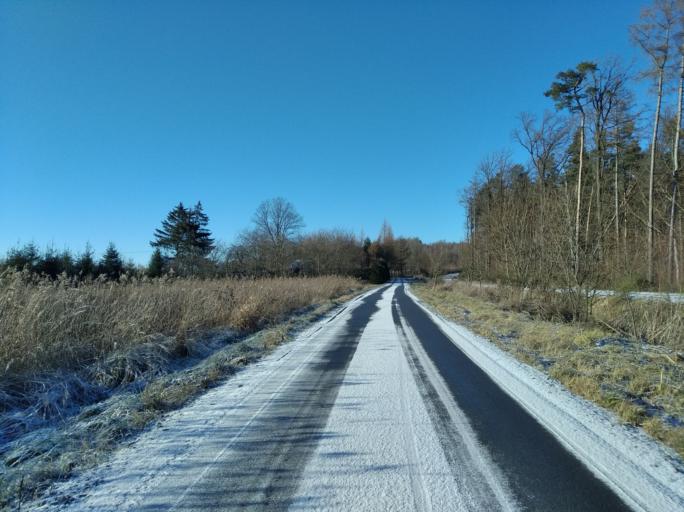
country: PL
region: Subcarpathian Voivodeship
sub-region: Powiat strzyzowski
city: Czudec
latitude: 49.9707
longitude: 21.8102
